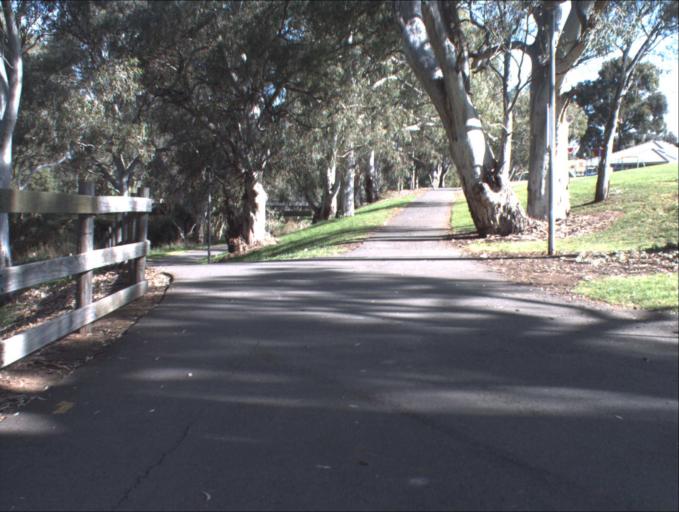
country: AU
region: South Australia
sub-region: Port Adelaide Enfield
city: Klemzig
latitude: -34.8813
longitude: 138.6478
